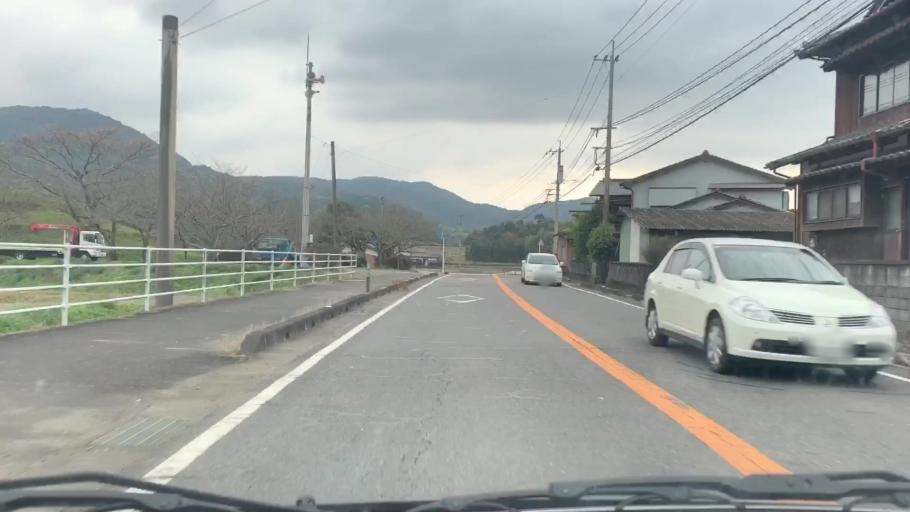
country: JP
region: Saga Prefecture
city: Takeocho-takeo
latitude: 33.1674
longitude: 130.0538
